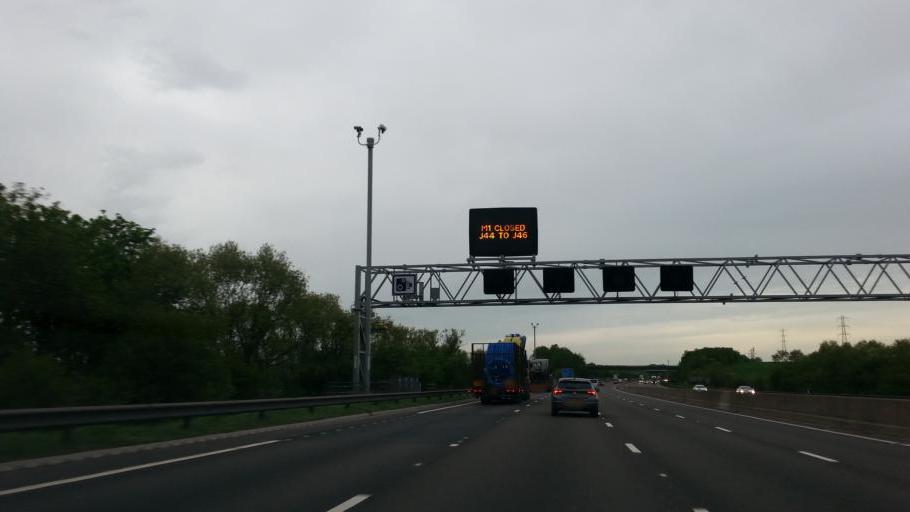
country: GB
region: England
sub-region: Derbyshire
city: Staveley
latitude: 53.2539
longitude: -1.3246
